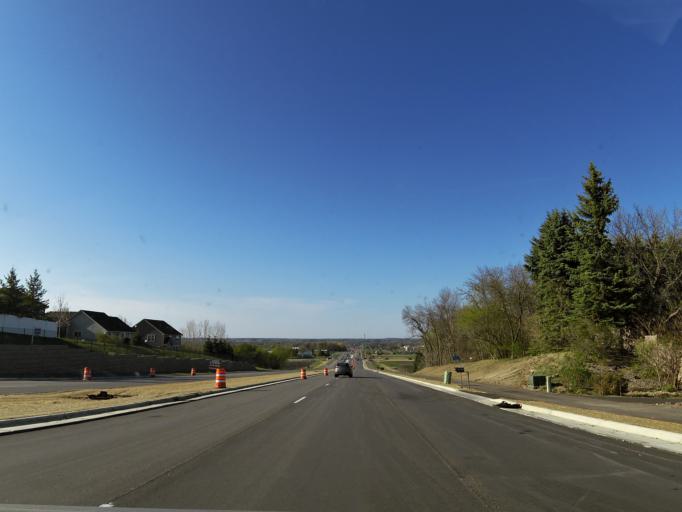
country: US
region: Minnesota
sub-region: Scott County
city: Shakopee
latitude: 44.7631
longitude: -93.5055
